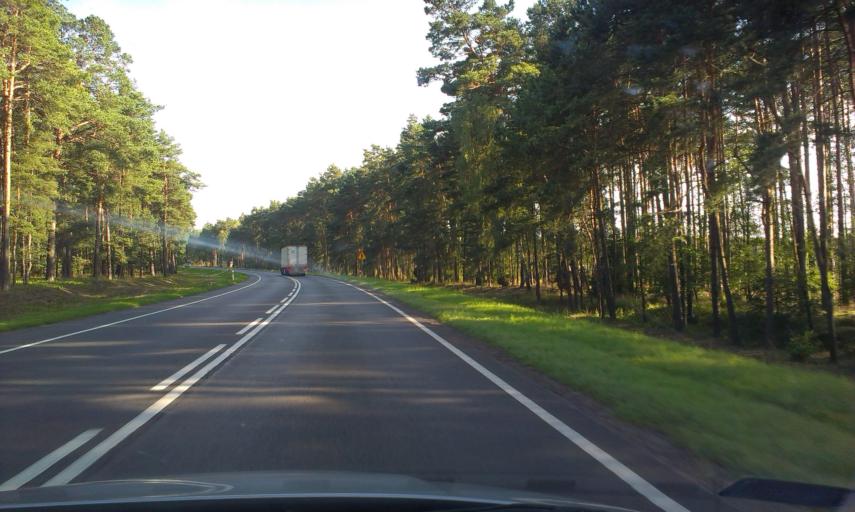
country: PL
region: Kujawsko-Pomorskie
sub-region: Powiat bydgoski
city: Biale Blota
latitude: 53.1087
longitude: 17.8846
